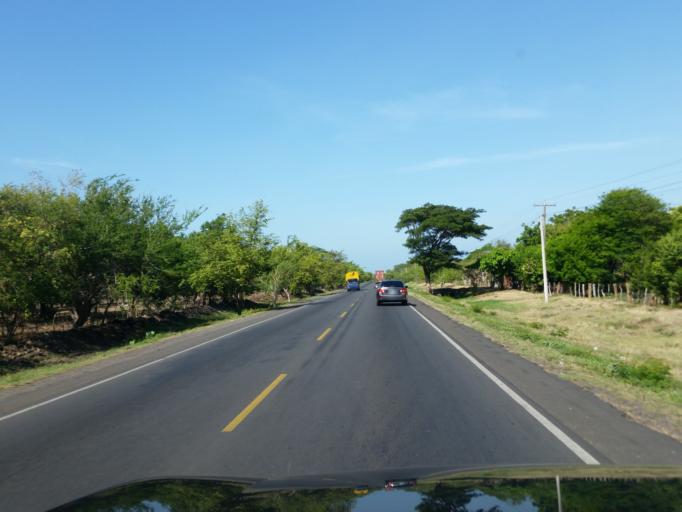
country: NI
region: Leon
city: La Paz Centro
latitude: 12.3187
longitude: -86.6946
